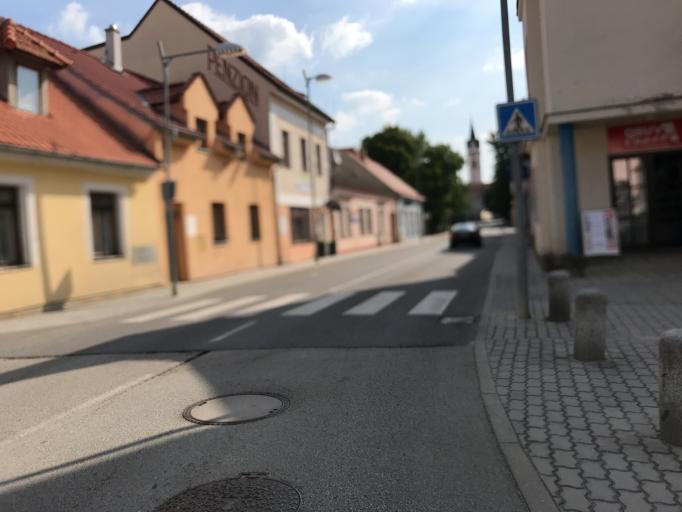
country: CZ
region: Jihocesky
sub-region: Okres Jindrichuv Hradec
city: Trebon
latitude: 49.0041
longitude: 14.7654
